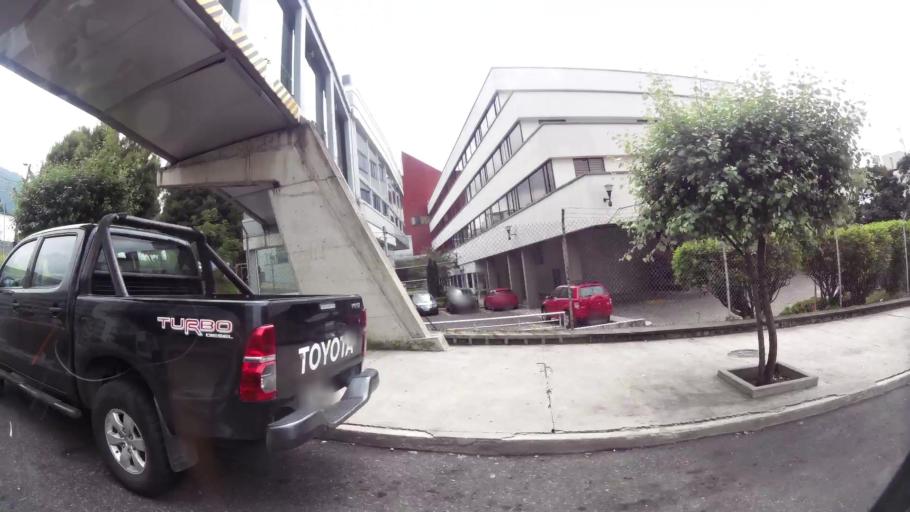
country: EC
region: Pichincha
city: Quito
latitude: -0.1853
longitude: -78.5040
